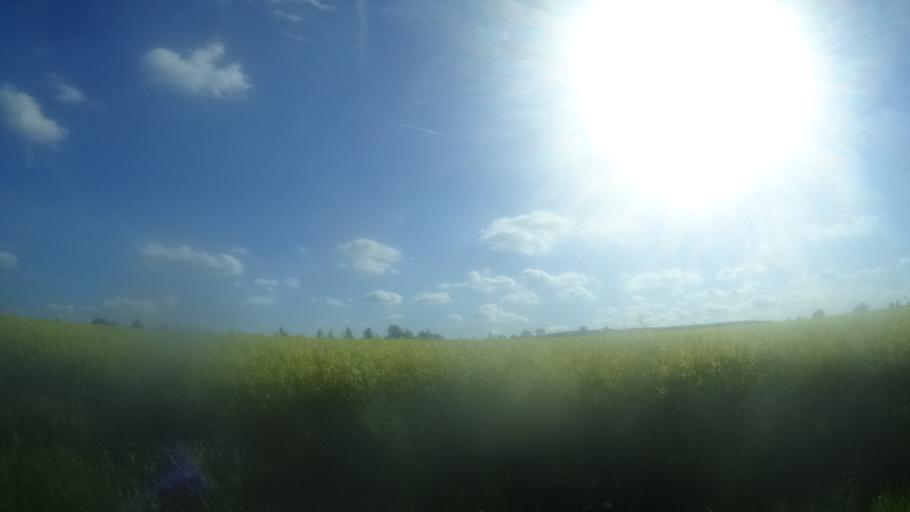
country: DE
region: Thuringia
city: Drobischau
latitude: 50.6372
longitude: 11.0873
